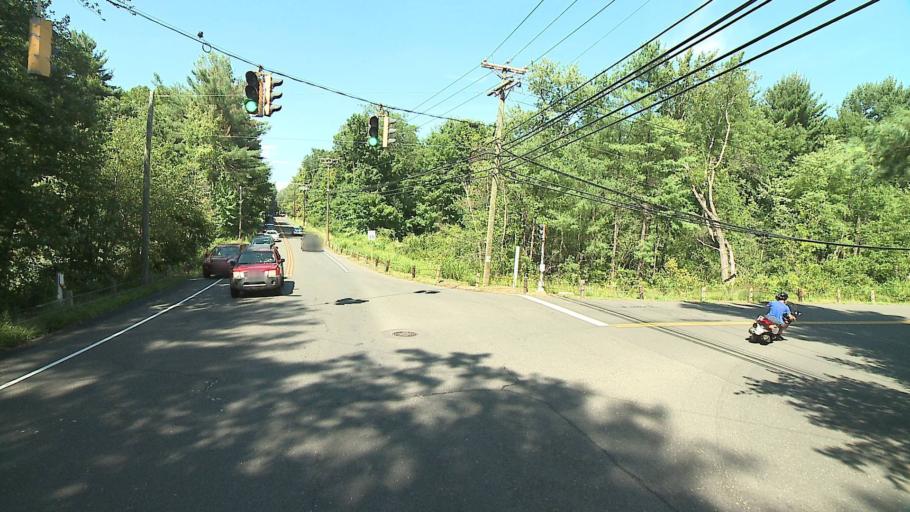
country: US
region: Connecticut
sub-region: Hartford County
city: Weatogue
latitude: 41.8257
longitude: -72.8569
